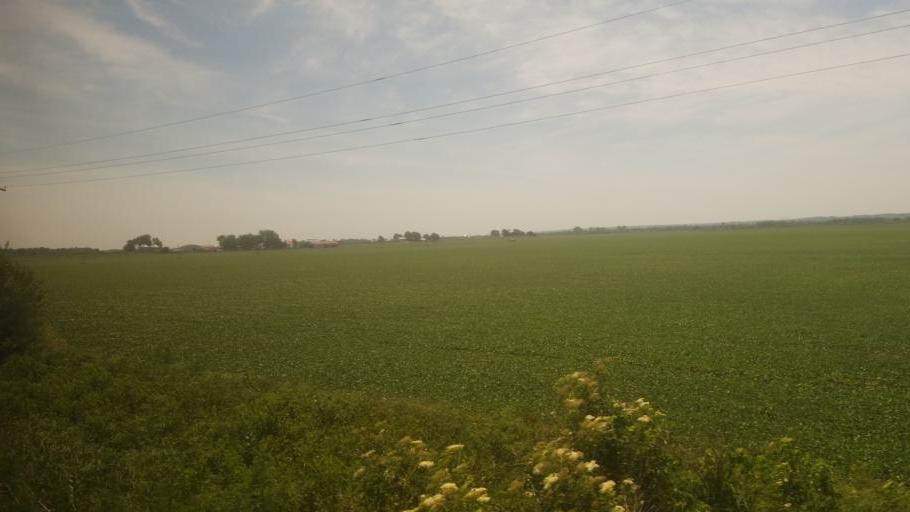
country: US
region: Missouri
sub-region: Carroll County
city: Carrollton
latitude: 39.2987
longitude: -93.7001
